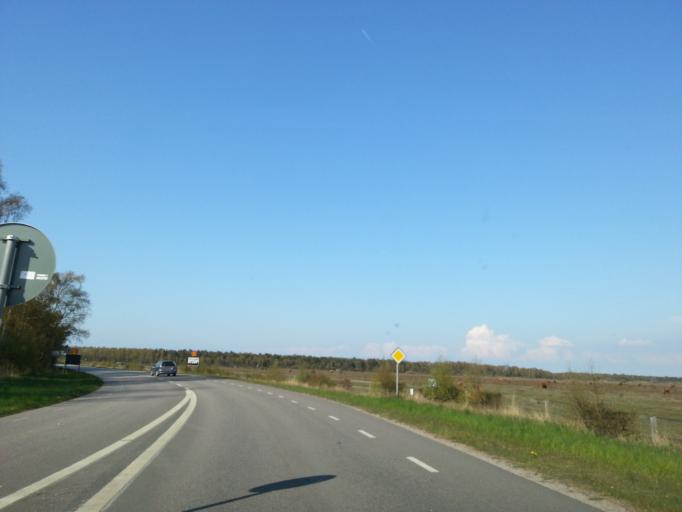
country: SE
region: Skane
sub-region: Vellinge Kommun
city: Skanor med Falsterbo
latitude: 55.4003
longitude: 12.8646
